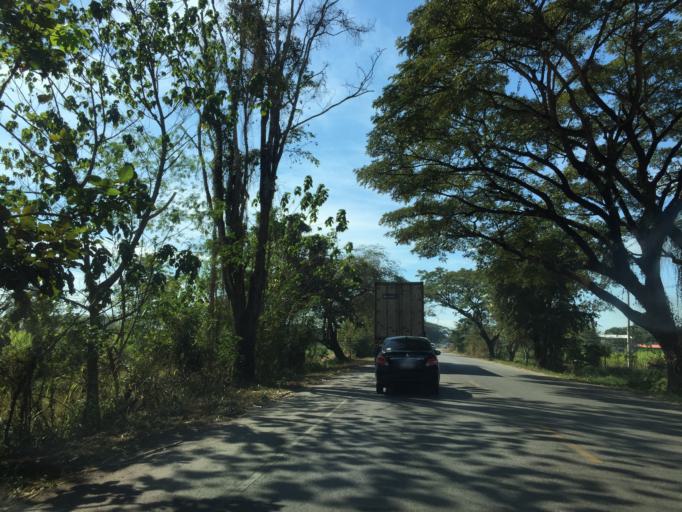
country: TH
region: Changwat Nong Bua Lamphu
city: Na Wang
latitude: 17.3212
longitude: 102.1125
